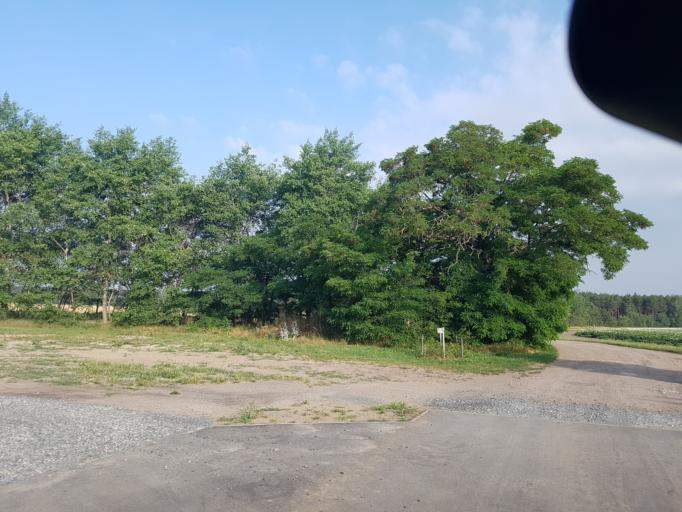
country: DE
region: Saxony-Anhalt
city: Holzdorf
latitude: 51.8602
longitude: 13.0996
